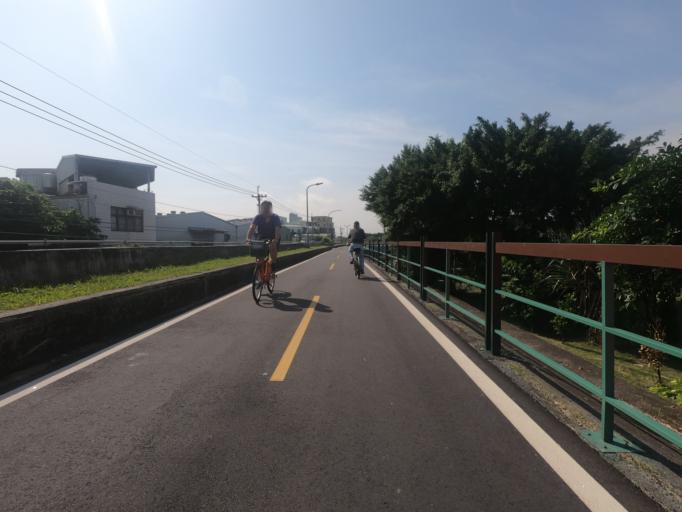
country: TW
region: Taipei
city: Taipei
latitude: 25.0968
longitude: 121.4933
